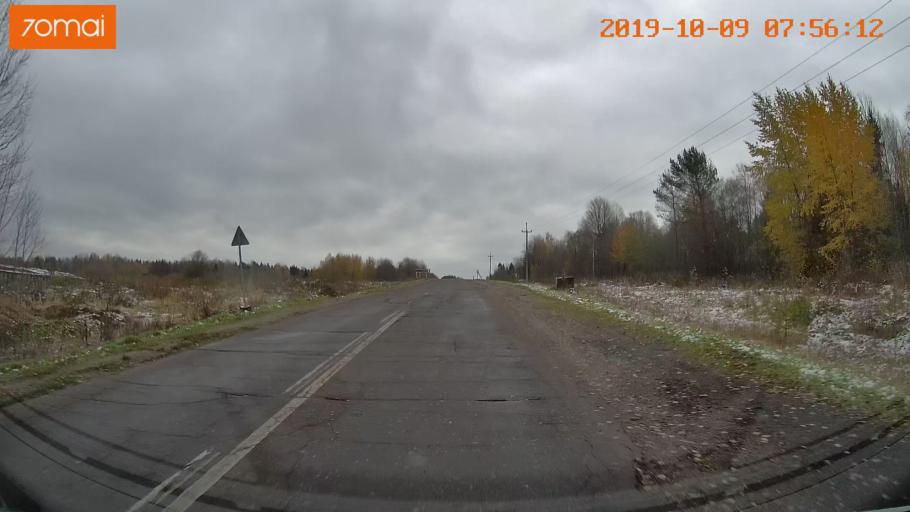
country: RU
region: Jaroslavl
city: Kukoboy
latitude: 58.6984
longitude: 39.9322
